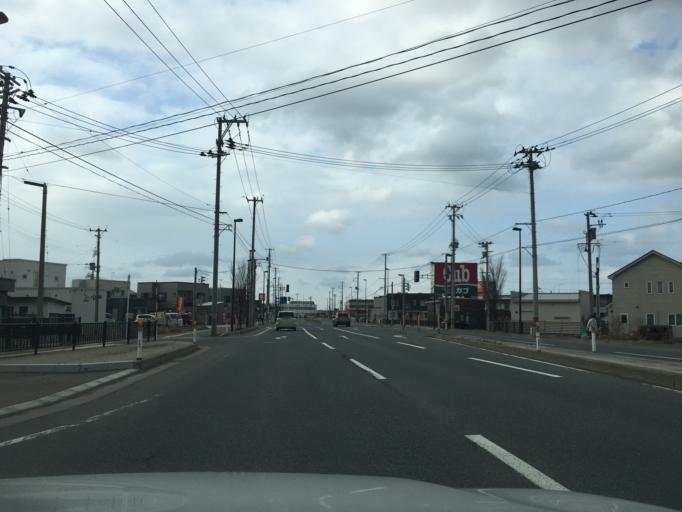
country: JP
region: Aomori
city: Aomori Shi
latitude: 40.8284
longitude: 140.7032
